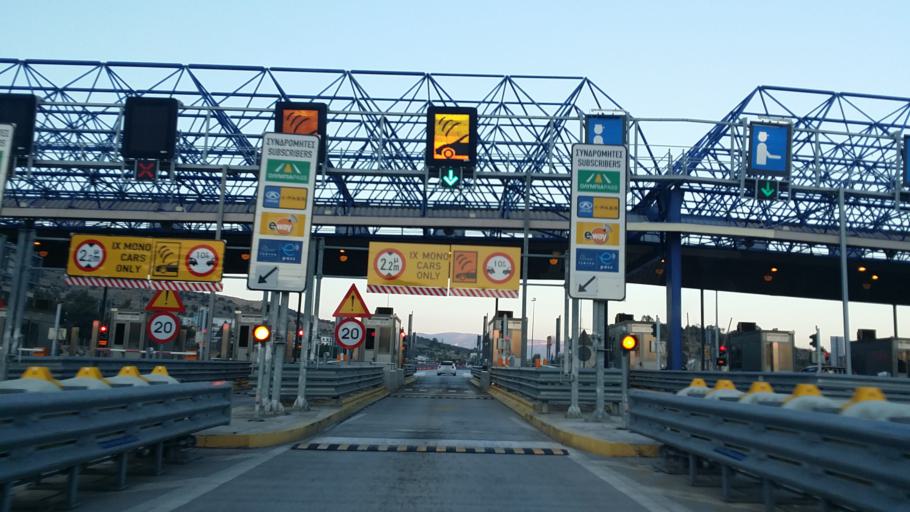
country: GR
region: Attica
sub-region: Nomarchia Dytikis Attikis
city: Mandra
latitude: 38.0420
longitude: 23.4954
